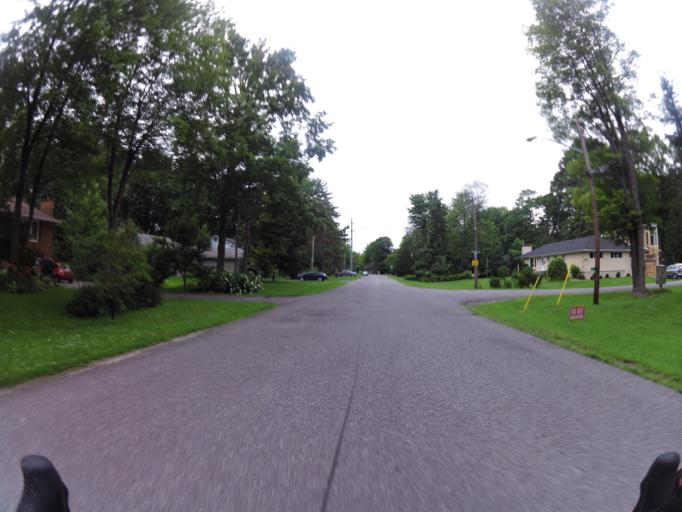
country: CA
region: Ontario
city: Ottawa
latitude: 45.3202
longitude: -75.7182
